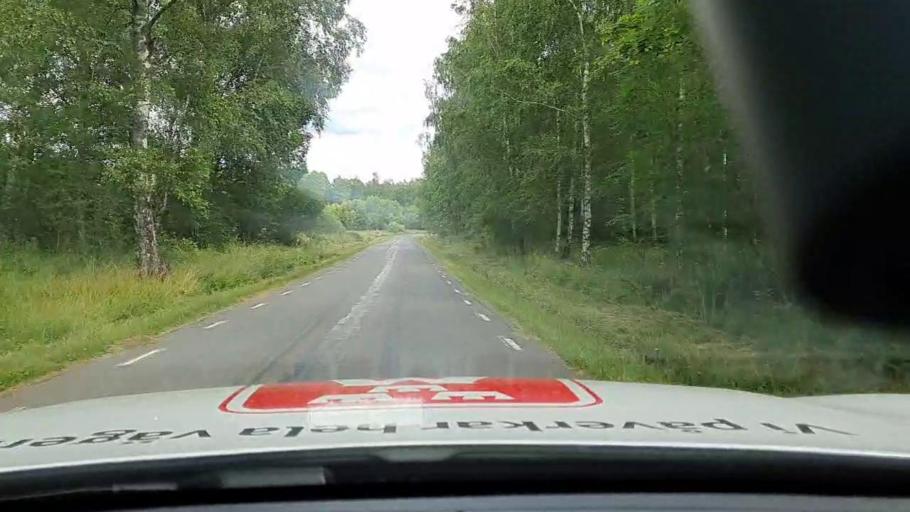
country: SE
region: Vaestra Goetaland
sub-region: Karlsborgs Kommun
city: Molltorp
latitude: 58.6116
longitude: 14.3544
